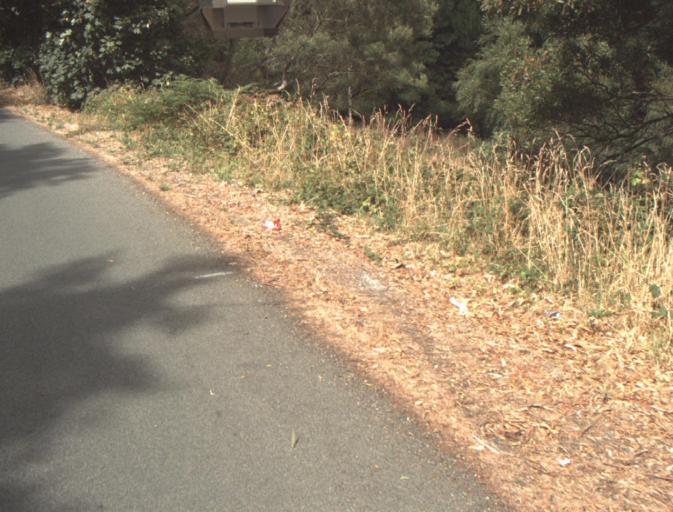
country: AU
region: Tasmania
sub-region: Dorset
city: Bridport
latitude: -41.1723
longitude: 147.2300
